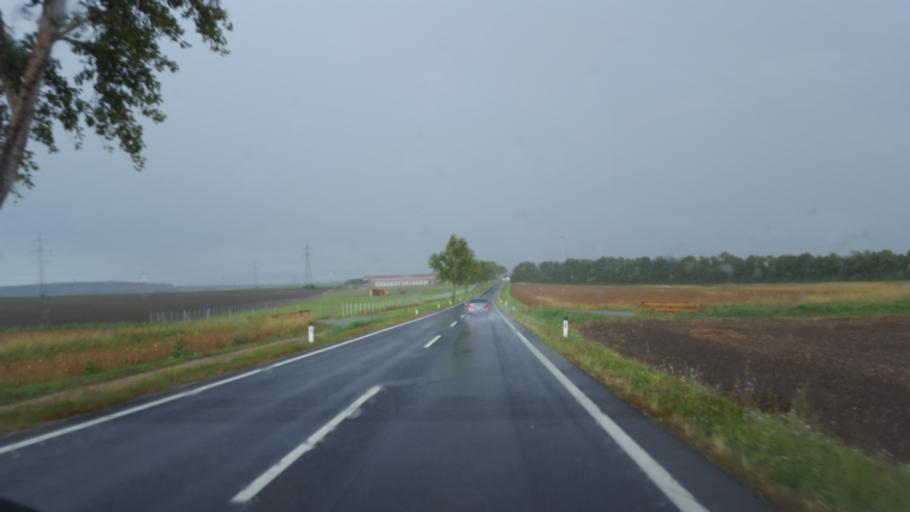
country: AT
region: Lower Austria
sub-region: Politischer Bezirk Bruck an der Leitha
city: Bruck an der Leitha
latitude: 48.0355
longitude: 16.7455
